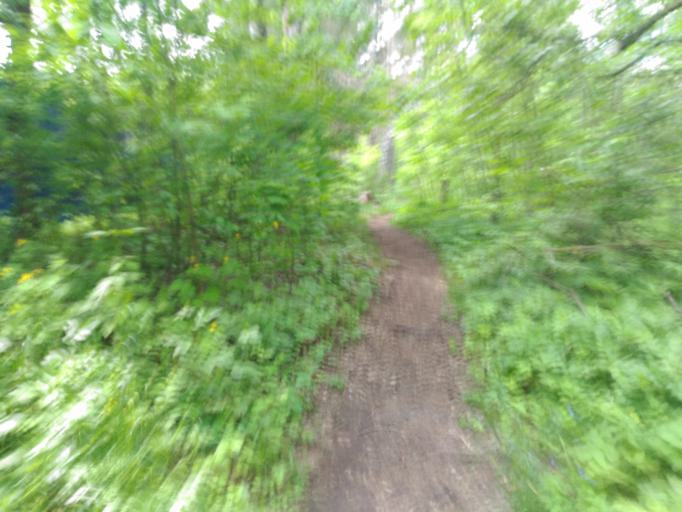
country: RU
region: Moscow
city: Rublevo
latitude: 55.7729
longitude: 37.3620
